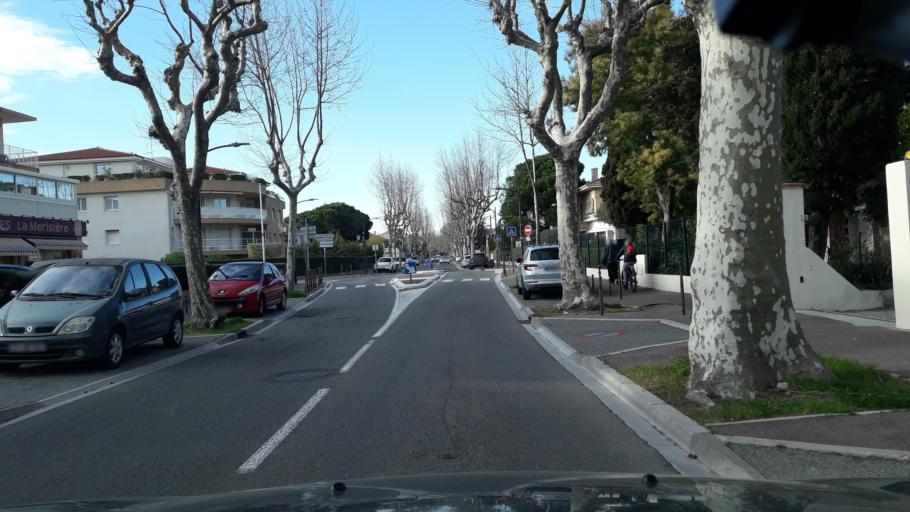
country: FR
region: Provence-Alpes-Cote d'Azur
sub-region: Departement du Var
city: Frejus
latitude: 43.4219
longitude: 6.7429
